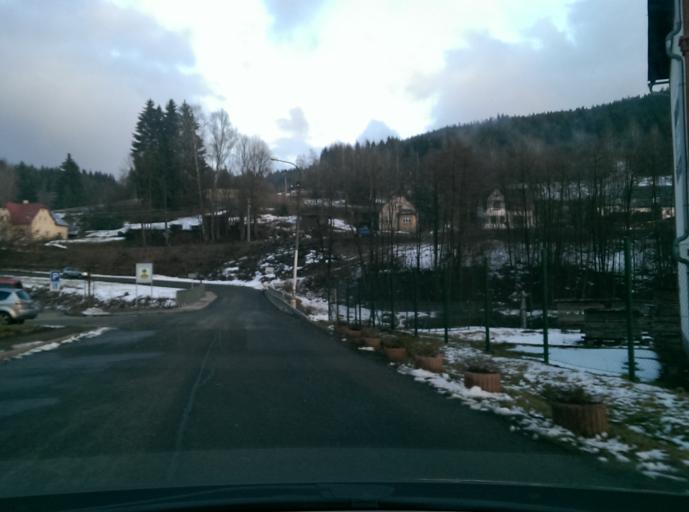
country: CZ
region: Liberecky
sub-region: Okres Jablonec nad Nisou
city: Smrzovka
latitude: 50.7571
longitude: 15.2663
